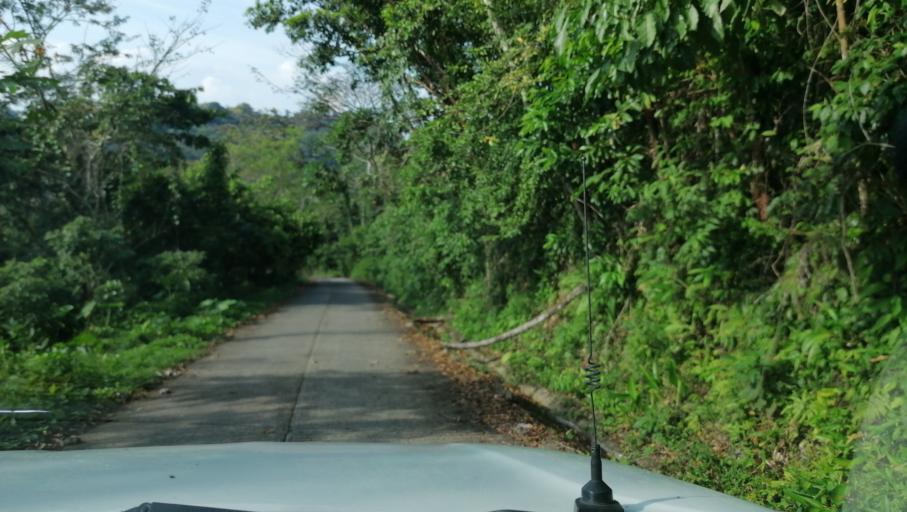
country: MX
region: Chiapas
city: Ostuacan
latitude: 17.4699
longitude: -93.2349
